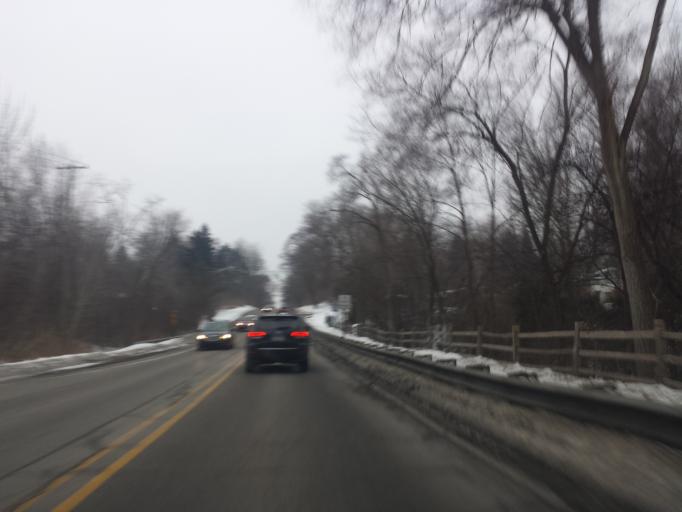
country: US
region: Michigan
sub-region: Oakland County
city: Franklin
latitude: 42.5124
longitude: -83.3398
